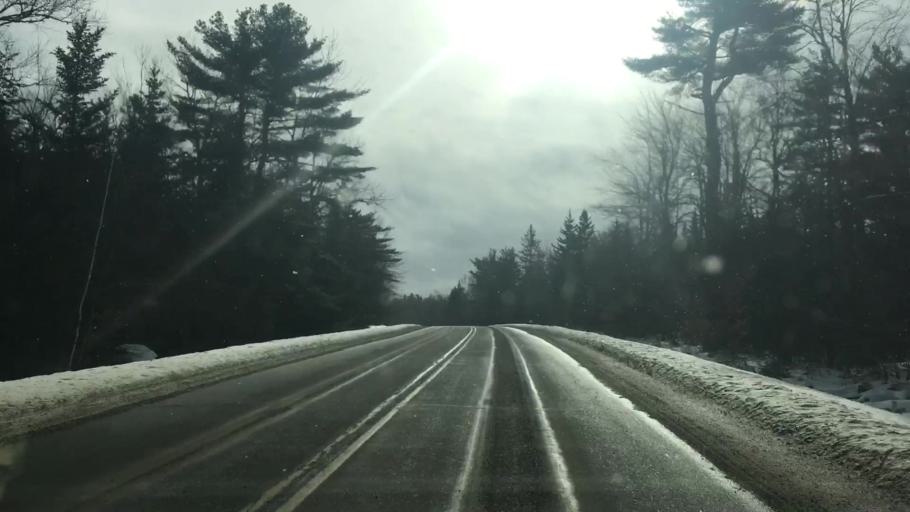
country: US
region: Maine
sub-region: Washington County
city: Calais
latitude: 45.0655
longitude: -67.3299
